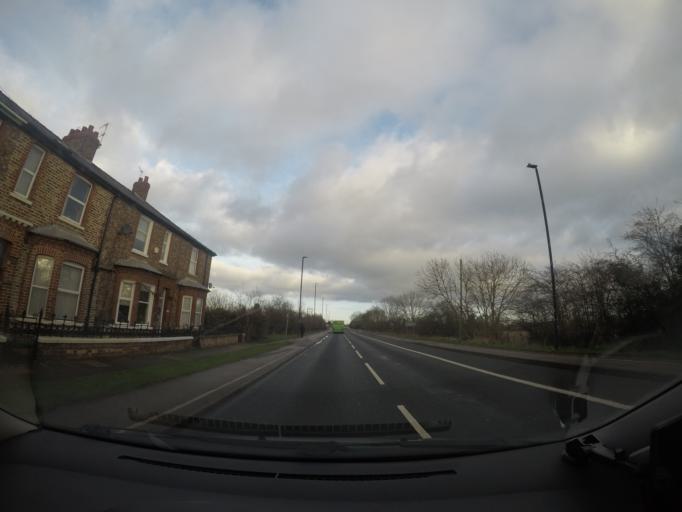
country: GB
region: England
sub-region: City of York
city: Huntington
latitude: 53.9758
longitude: -1.0572
